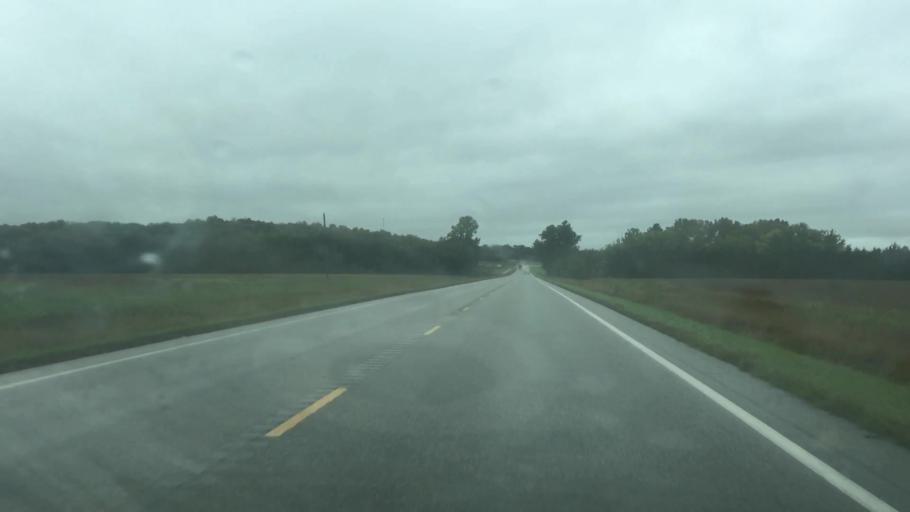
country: US
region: Kansas
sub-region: Anderson County
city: Garnett
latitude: 38.3734
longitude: -95.1154
